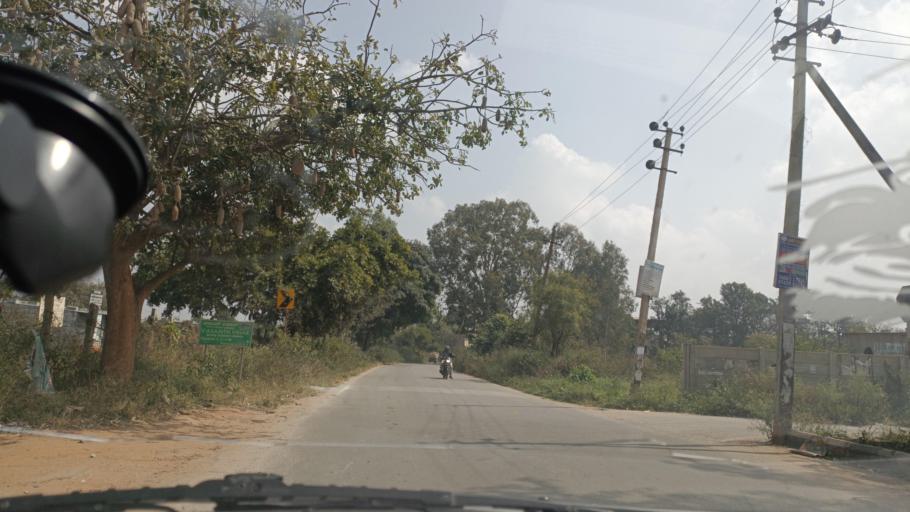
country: IN
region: Karnataka
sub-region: Bangalore Urban
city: Yelahanka
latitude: 13.1605
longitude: 77.6369
